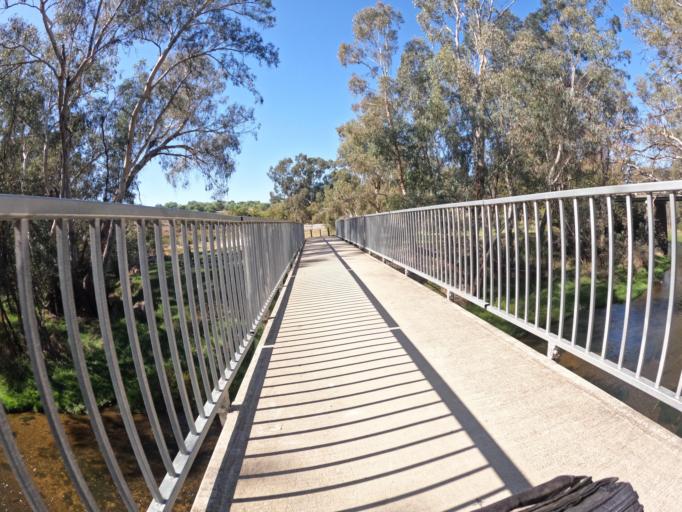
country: AU
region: Victoria
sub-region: Greater Bendigo
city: Epsom
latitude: -36.7904
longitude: 144.5084
